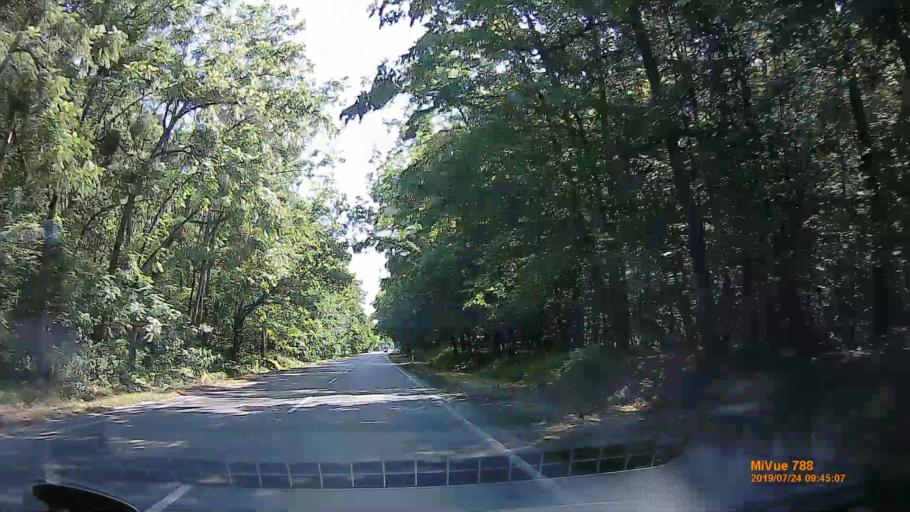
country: HU
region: Szabolcs-Szatmar-Bereg
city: Baktaloranthaza
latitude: 47.9843
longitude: 22.0627
